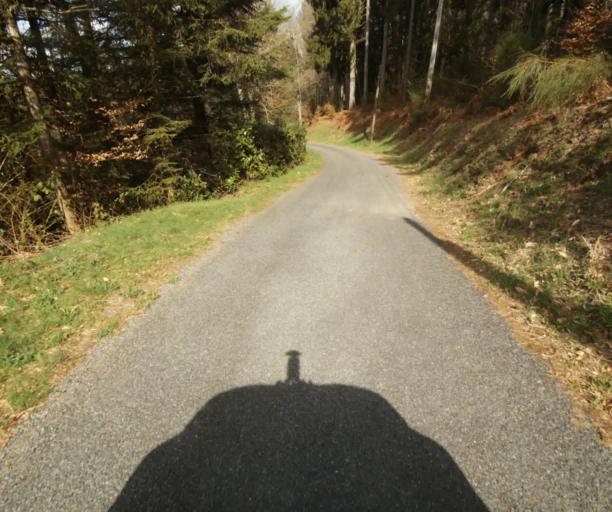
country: FR
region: Limousin
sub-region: Departement de la Correze
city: Correze
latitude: 45.3586
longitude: 1.8760
